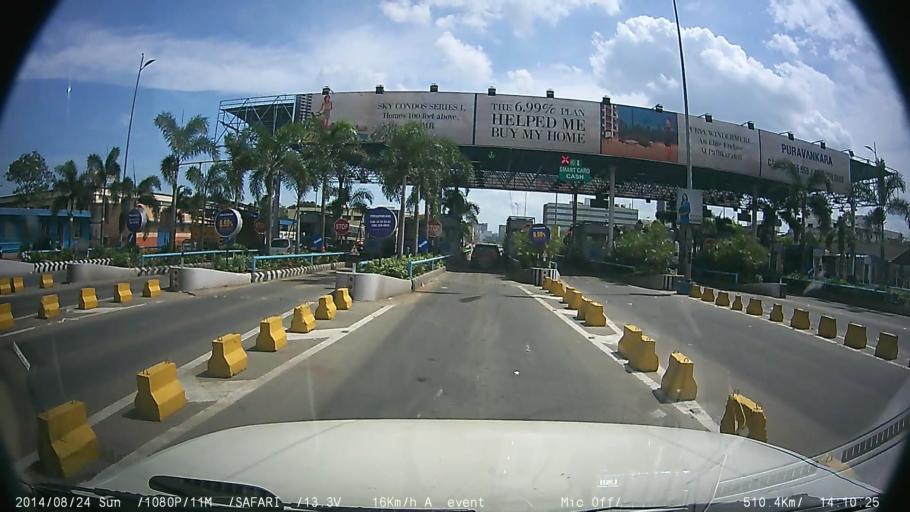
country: IN
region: Tamil Nadu
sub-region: Kancheepuram
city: Perungudi
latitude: 12.9570
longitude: 80.2438
